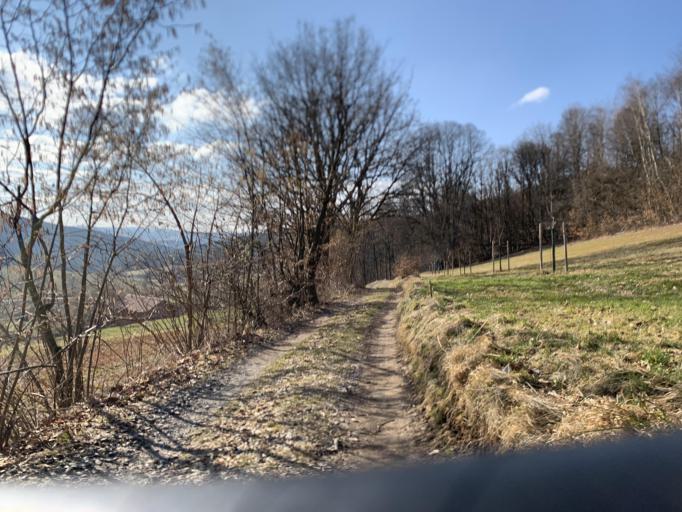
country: DE
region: Bavaria
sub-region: Upper Palatinate
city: Thanstein
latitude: 49.3778
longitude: 12.4410
